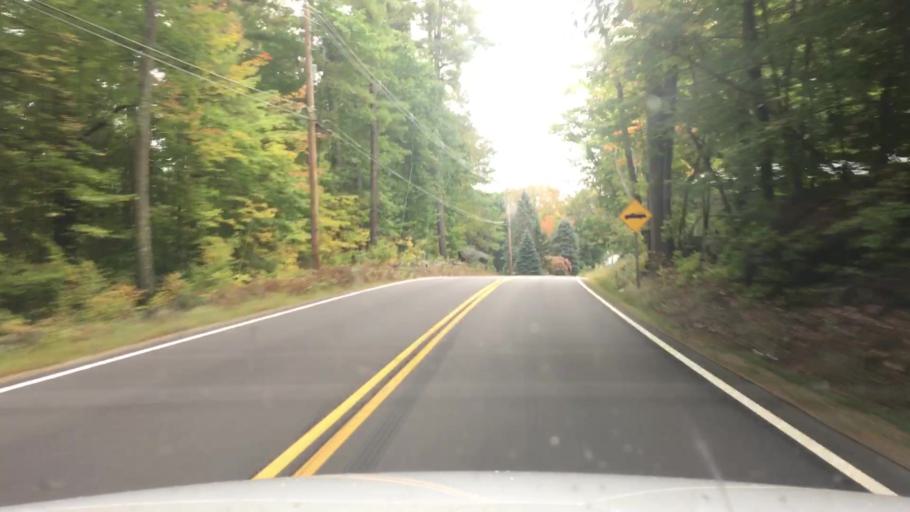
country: US
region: New Hampshire
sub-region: Carroll County
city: Wolfeboro
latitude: 43.5446
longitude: -71.3027
